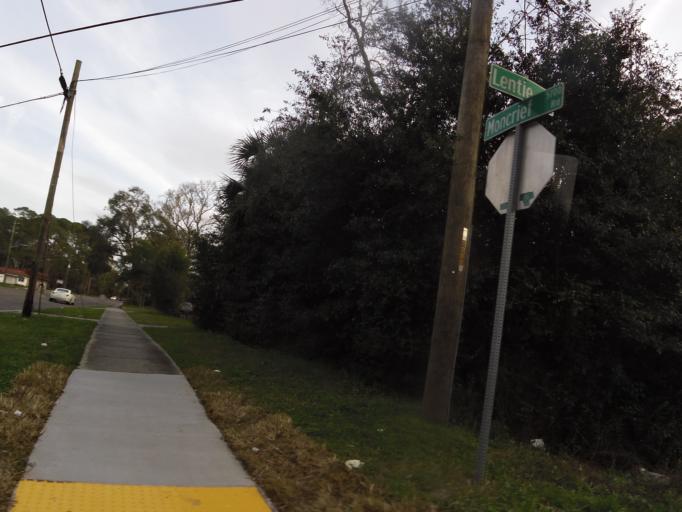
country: US
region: Florida
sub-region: Duval County
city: Jacksonville
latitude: 30.3778
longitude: -81.6926
